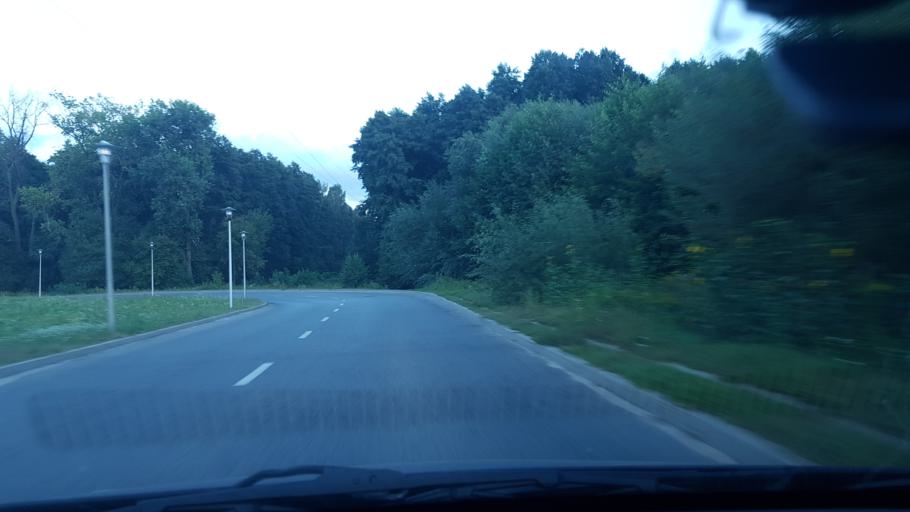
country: PL
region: Masovian Voivodeship
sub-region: Warszawa
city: Targowek
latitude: 52.3019
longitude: 21.0756
